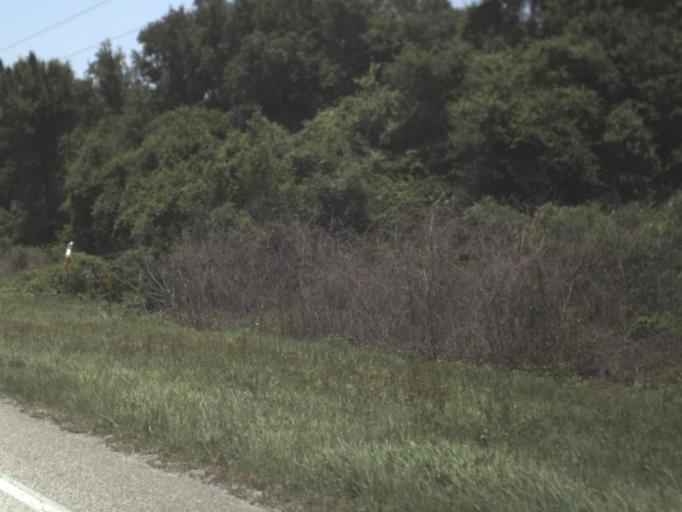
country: US
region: Florida
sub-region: Bradford County
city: Starke
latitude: 30.0960
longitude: -82.0564
